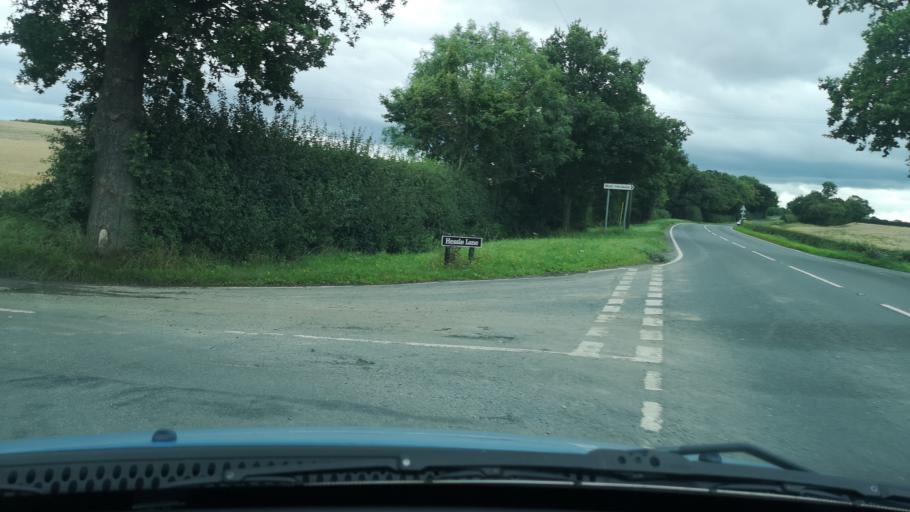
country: GB
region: England
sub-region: City and Borough of Wakefield
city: Featherstone
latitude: 53.6571
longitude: -1.3585
